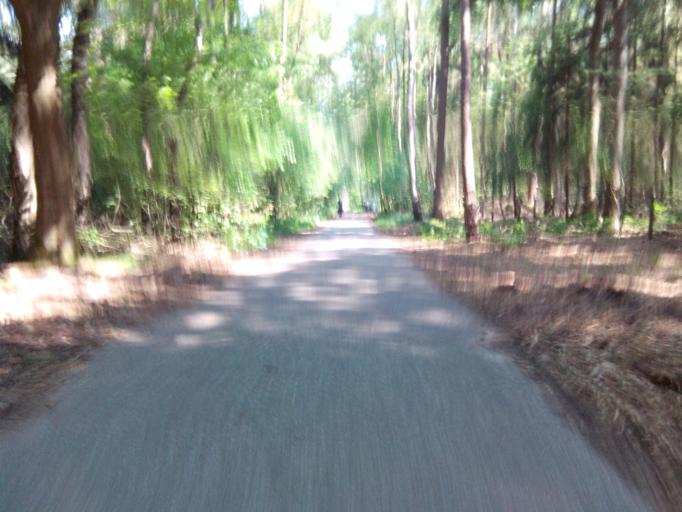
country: NL
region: Utrecht
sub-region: Gemeente Utrechtse Heuvelrug
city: Leersum
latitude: 52.0217
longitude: 5.4340
